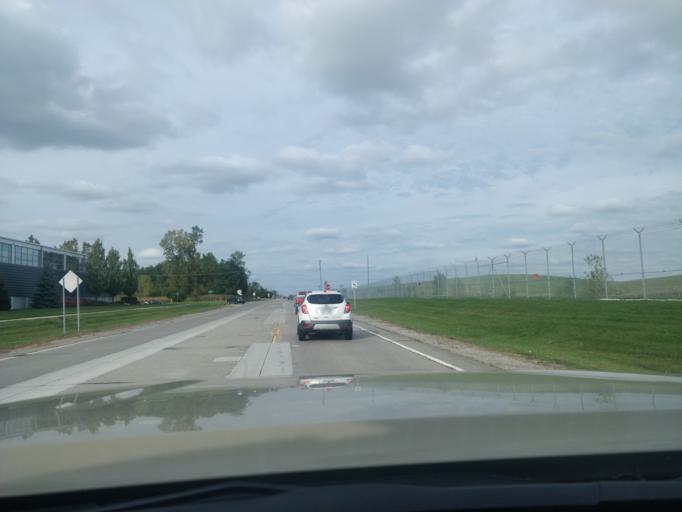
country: US
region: Michigan
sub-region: Wayne County
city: Romulus
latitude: 42.2073
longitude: -83.3866
